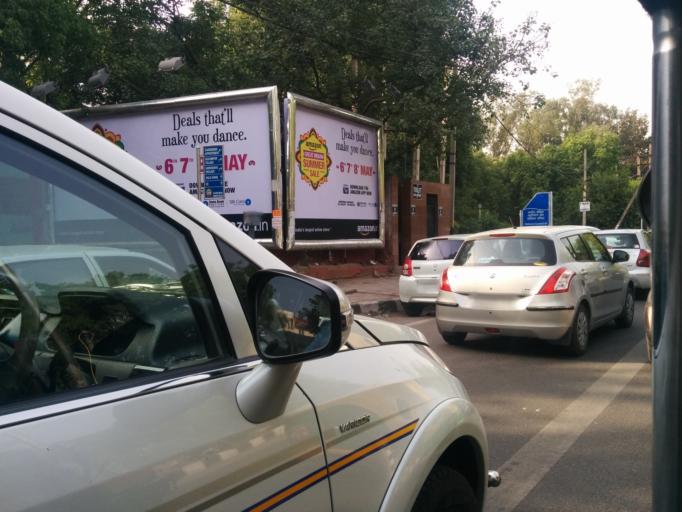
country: IN
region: NCT
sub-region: New Delhi
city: New Delhi
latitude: 28.5385
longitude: 77.1985
